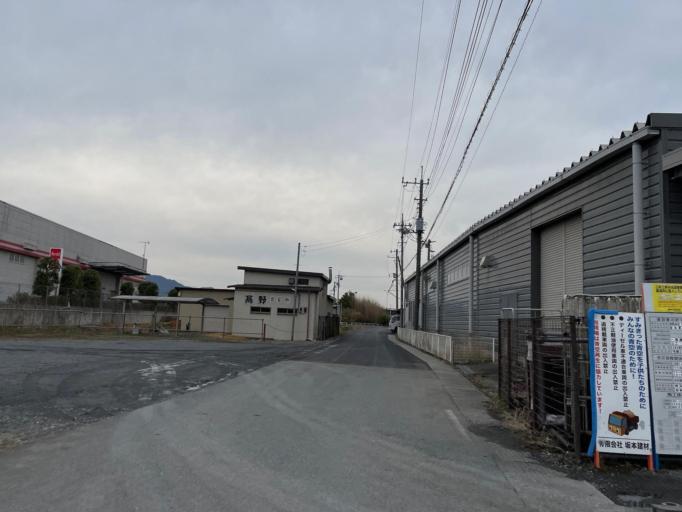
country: JP
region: Saitama
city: Kodamacho-kodamaminami
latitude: 36.2003
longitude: 139.1306
